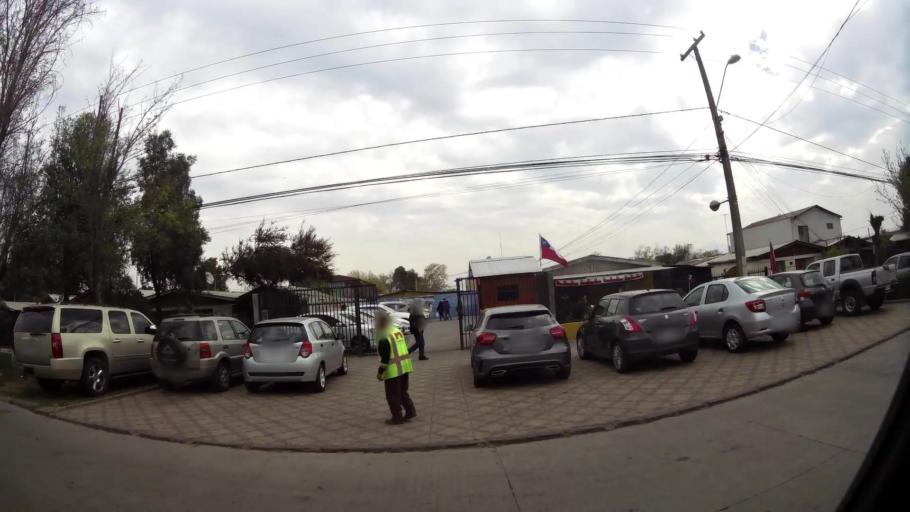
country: CL
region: Santiago Metropolitan
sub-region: Provincia de Santiago
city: Lo Prado
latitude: -33.5015
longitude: -70.7688
